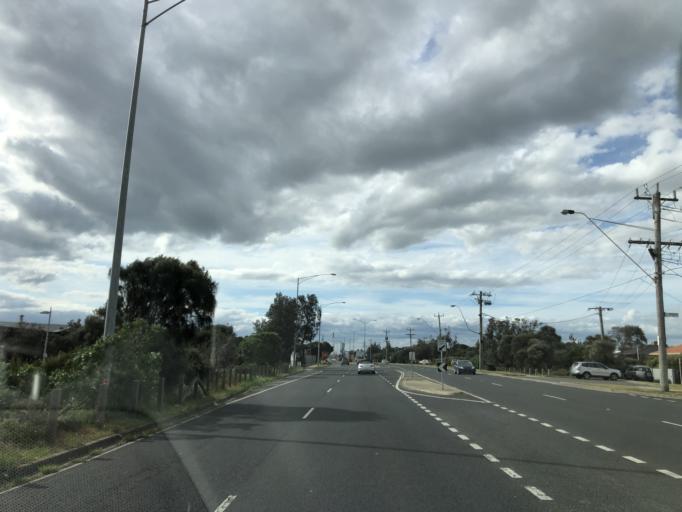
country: AU
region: Victoria
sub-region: Kingston
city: Carrum
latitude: -38.0862
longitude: 145.1247
